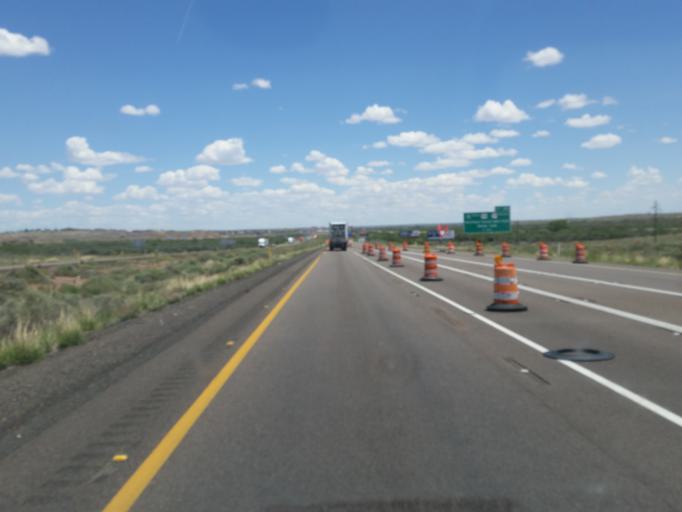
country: US
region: Arizona
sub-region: Navajo County
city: Holbrook
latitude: 34.9069
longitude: -110.2092
